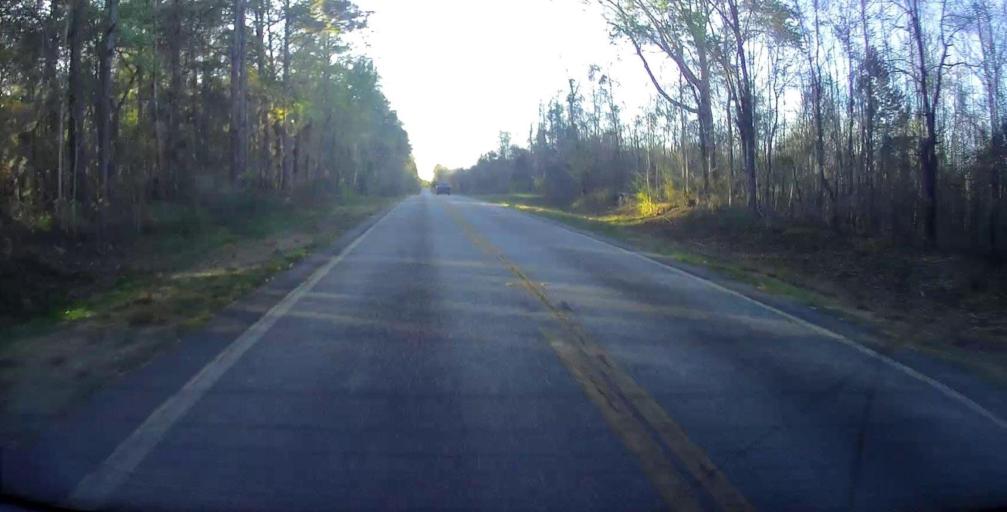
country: US
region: Georgia
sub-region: Wilcox County
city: Abbeville
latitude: 32.1056
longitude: -83.3101
